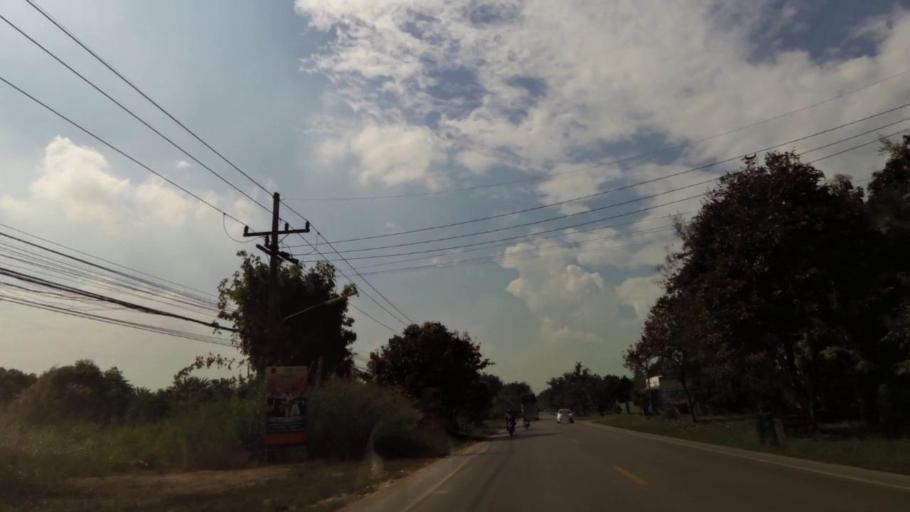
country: TH
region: Chiang Rai
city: Mae Lao
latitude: 19.8569
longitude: 99.7586
